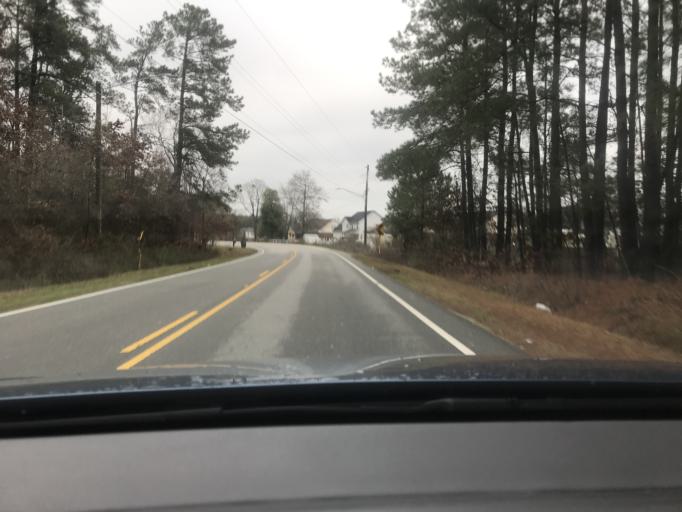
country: US
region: North Carolina
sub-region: Hoke County
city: Rockfish
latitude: 35.0297
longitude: -79.0073
